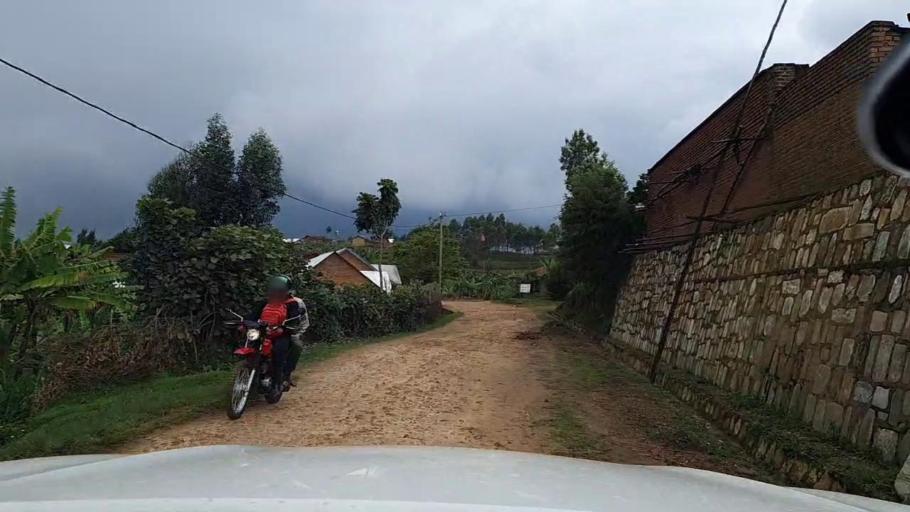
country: RW
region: Western Province
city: Kibuye
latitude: -2.1042
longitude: 29.4846
